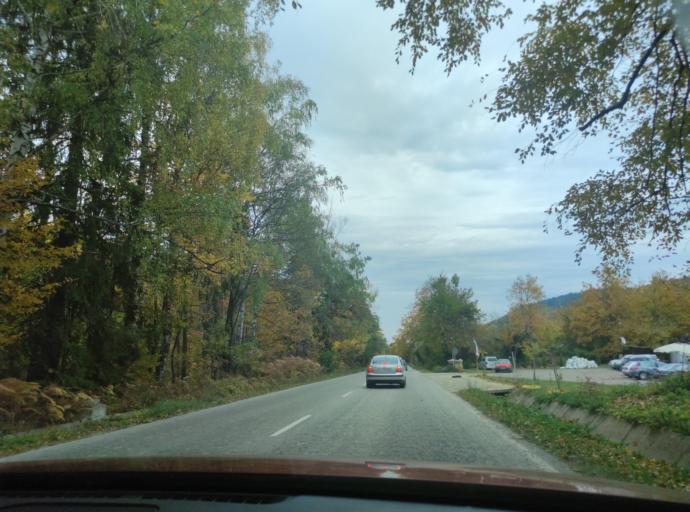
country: BG
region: Montana
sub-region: Obshtina Berkovitsa
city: Berkovitsa
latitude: 43.1821
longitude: 23.1561
